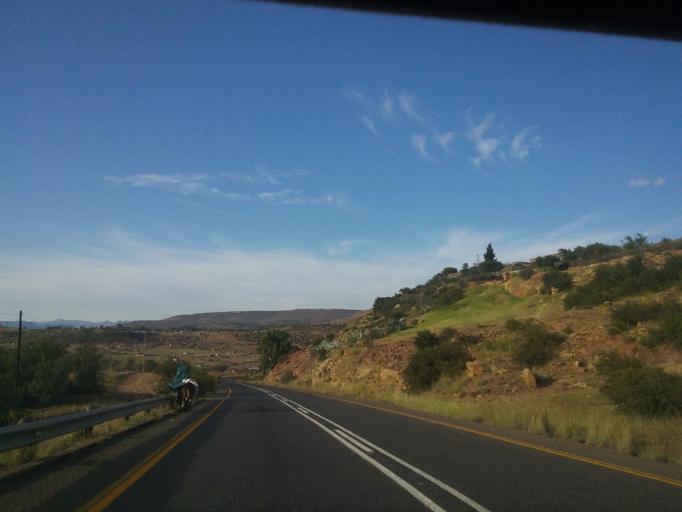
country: LS
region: Mohale's Hoek District
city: Mohale's Hoek
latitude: -30.2234
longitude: 27.4354
